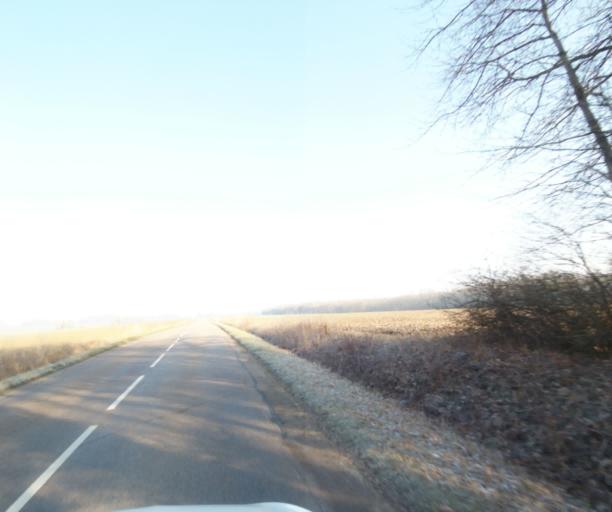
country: FR
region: Champagne-Ardenne
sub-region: Departement de la Haute-Marne
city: Montier-en-Der
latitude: 48.4317
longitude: 4.7525
